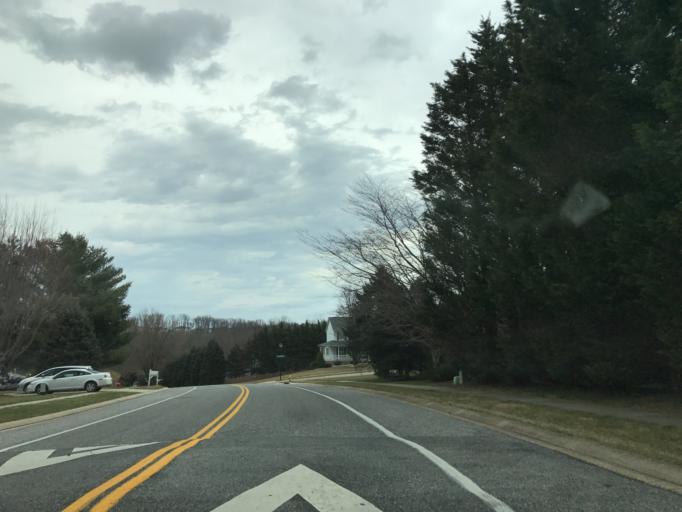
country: US
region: Maryland
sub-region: Harford County
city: South Bel Air
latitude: 39.5264
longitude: -76.3210
